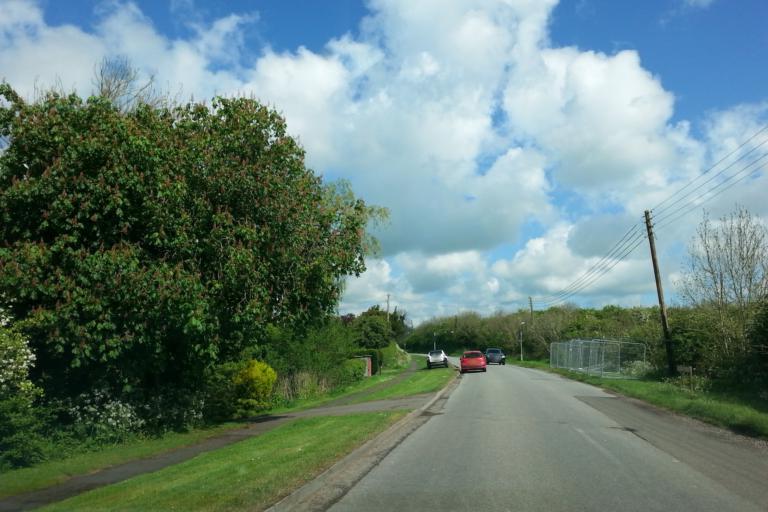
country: GB
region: England
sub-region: District of Rutland
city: Greetham
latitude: 52.8093
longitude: -0.6208
